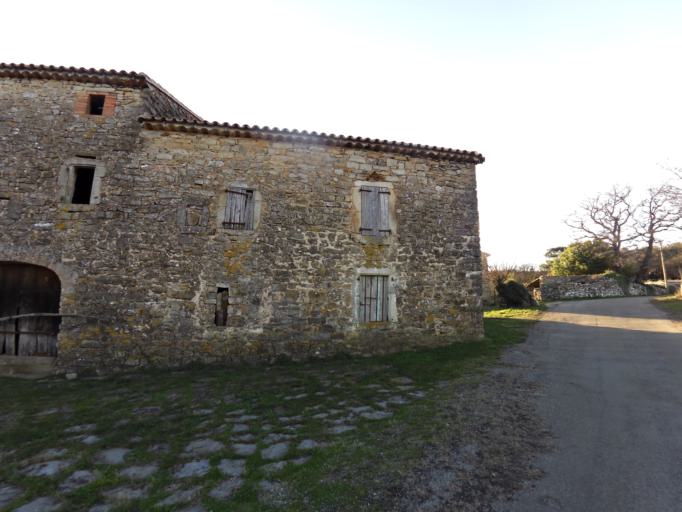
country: FR
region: Languedoc-Roussillon
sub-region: Departement du Gard
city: Anduze
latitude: 44.0350
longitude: 3.9284
